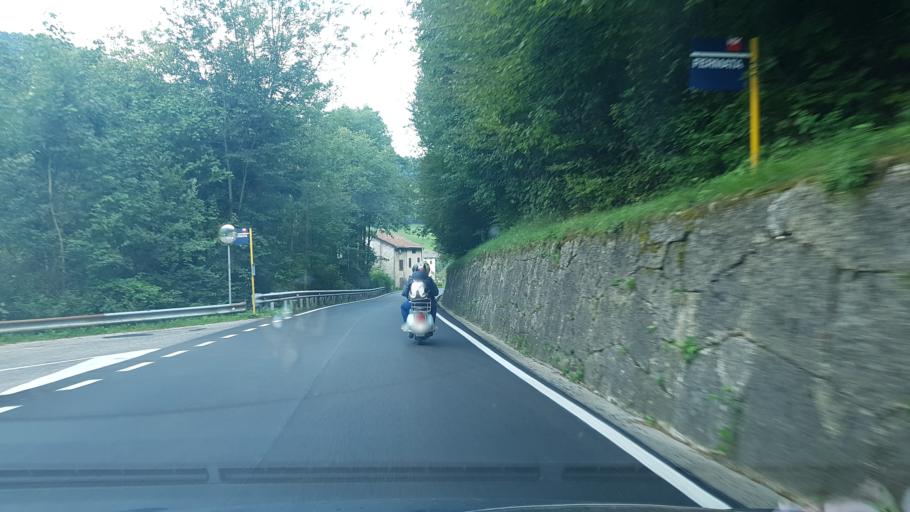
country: IT
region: Veneto
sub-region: Provincia di Vicenza
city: Valli del Pasubio
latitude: 45.7495
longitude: 11.2350
